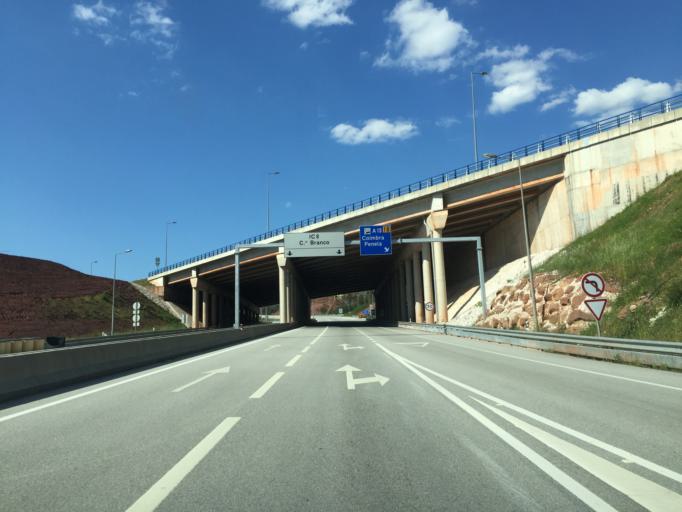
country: PT
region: Leiria
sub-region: Figueiro Dos Vinhos
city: Figueiro dos Vinhos
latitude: 39.9225
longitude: -8.3437
